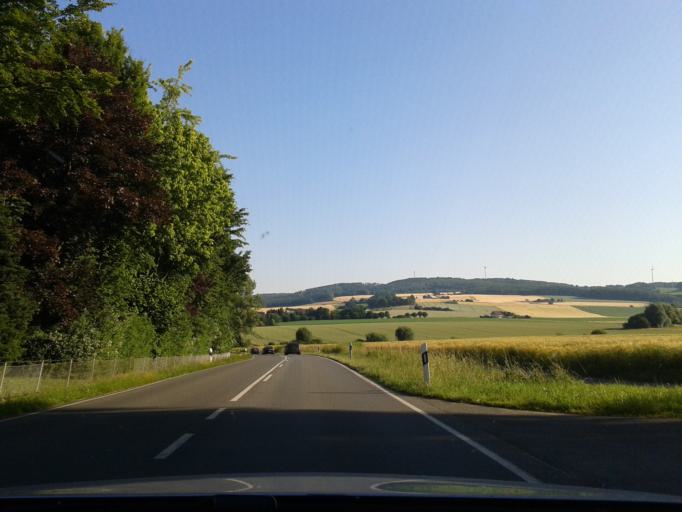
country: DE
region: North Rhine-Westphalia
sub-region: Regierungsbezirk Detmold
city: Barntrup
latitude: 52.0189
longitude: 9.0621
